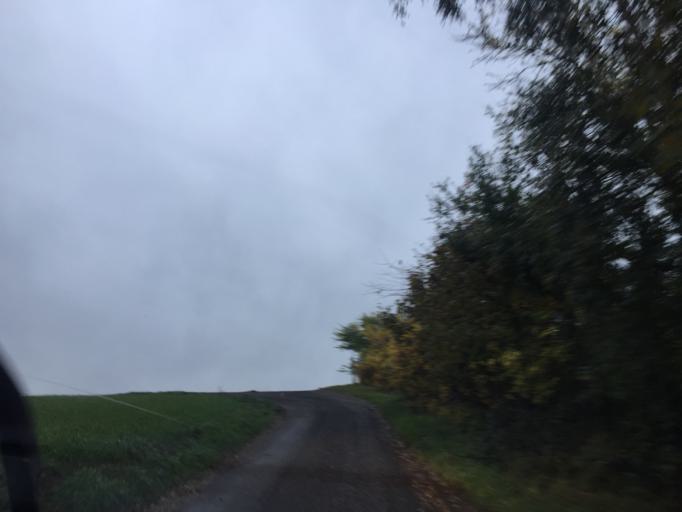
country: DK
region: Zealand
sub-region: Ringsted Kommune
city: Ringsted
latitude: 55.4840
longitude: 11.7423
